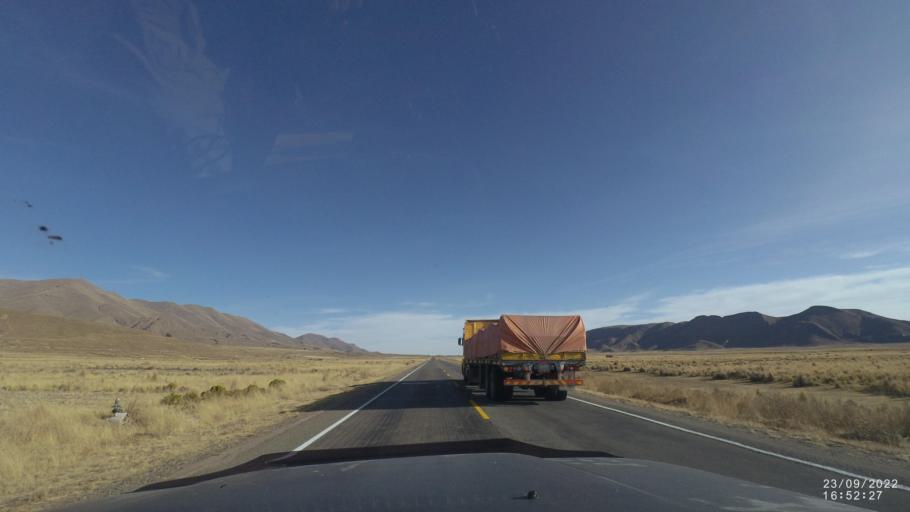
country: BO
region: Oruro
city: Poopo
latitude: -18.4316
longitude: -66.9734
